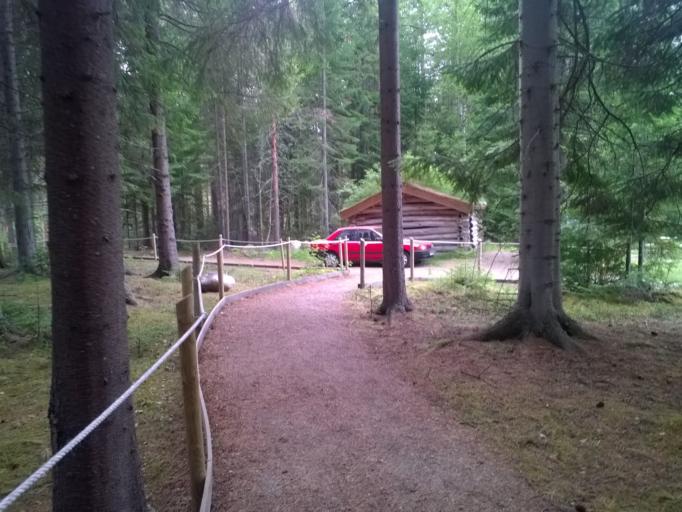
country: NO
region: Nordland
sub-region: Saltdal
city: Rognan
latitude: 66.8160
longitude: 15.3922
